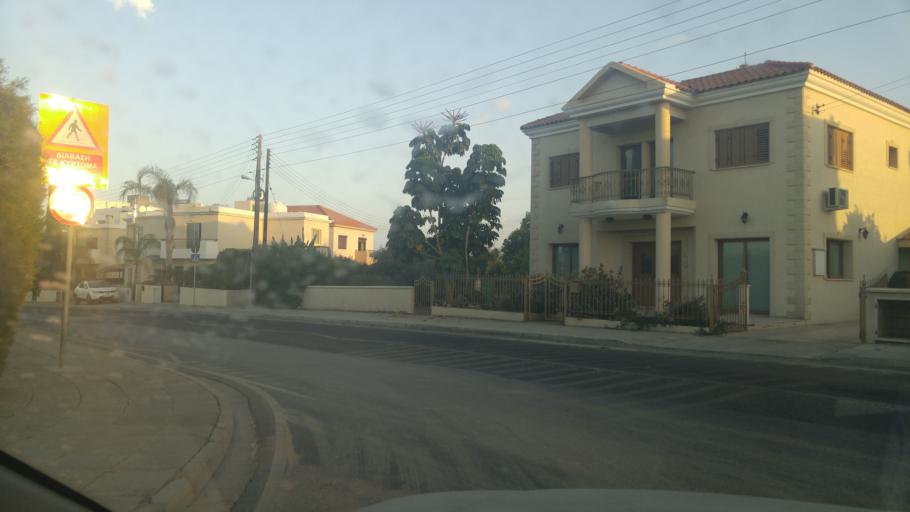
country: CY
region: Limassol
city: Ypsonas
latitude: 34.6870
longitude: 32.9700
